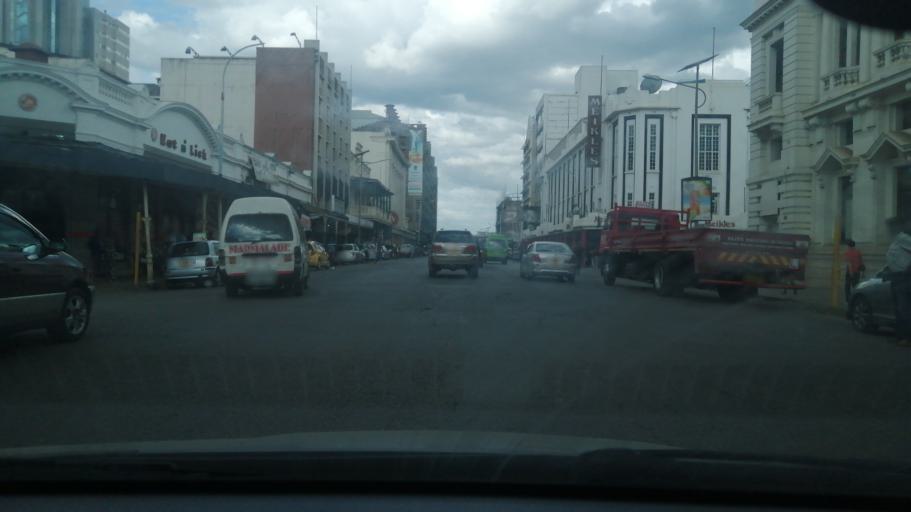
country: ZW
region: Harare
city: Harare
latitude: -17.8324
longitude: 31.0502
